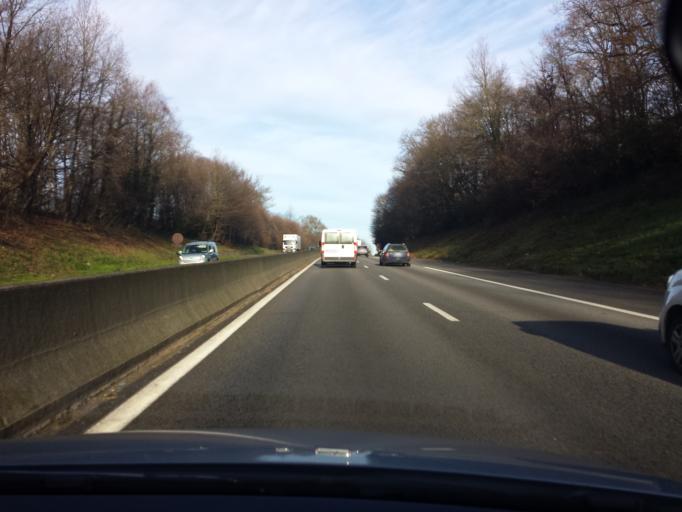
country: FR
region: Ile-de-France
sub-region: Departement des Yvelines
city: Chambourcy
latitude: 48.8969
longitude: 2.0064
